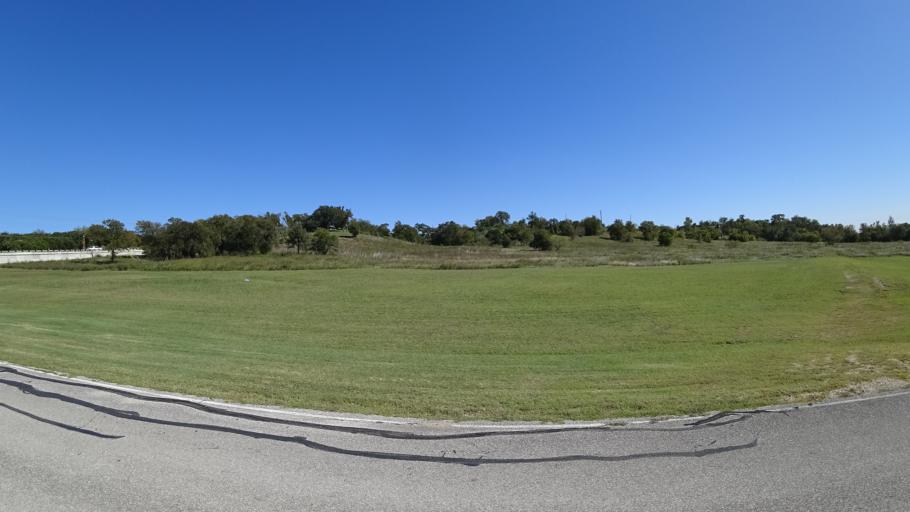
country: US
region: Texas
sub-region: Travis County
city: Hornsby Bend
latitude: 30.2777
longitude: -97.6425
